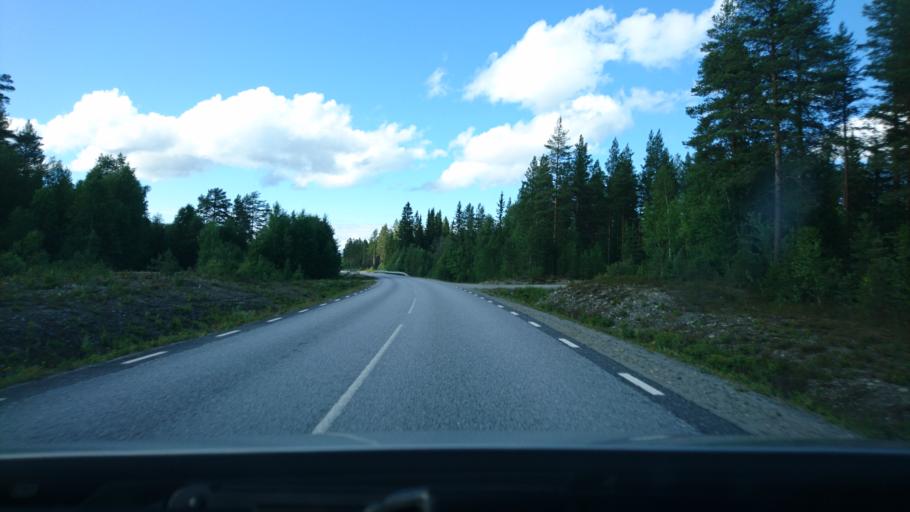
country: SE
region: Vaesterbotten
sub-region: Asele Kommun
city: Asele
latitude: 64.2746
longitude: 17.2742
